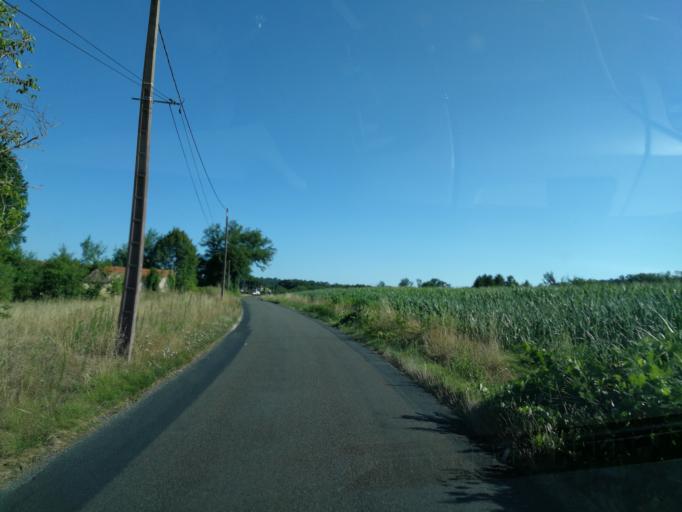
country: FR
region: Midi-Pyrenees
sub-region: Departement du Lot
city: Gourdon
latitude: 44.7942
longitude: 1.3680
